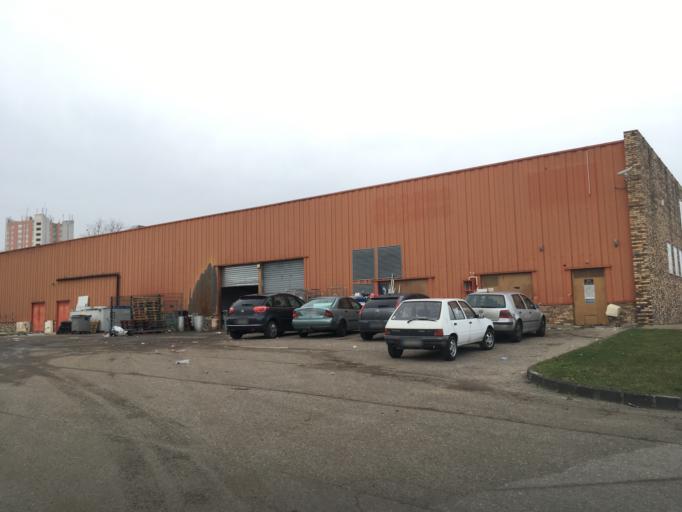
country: FR
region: Haute-Normandie
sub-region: Departement de l'Eure
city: Vernon
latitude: 49.0795
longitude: 1.4871
